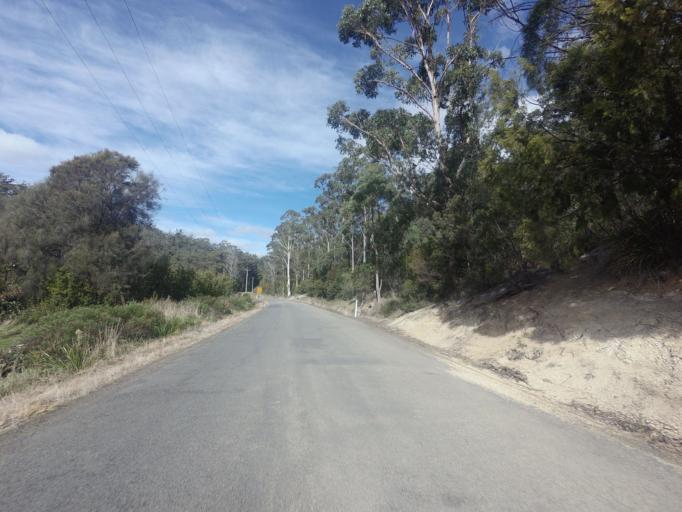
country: AU
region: Tasmania
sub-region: Clarence
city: Sandford
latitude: -43.1224
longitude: 147.7603
